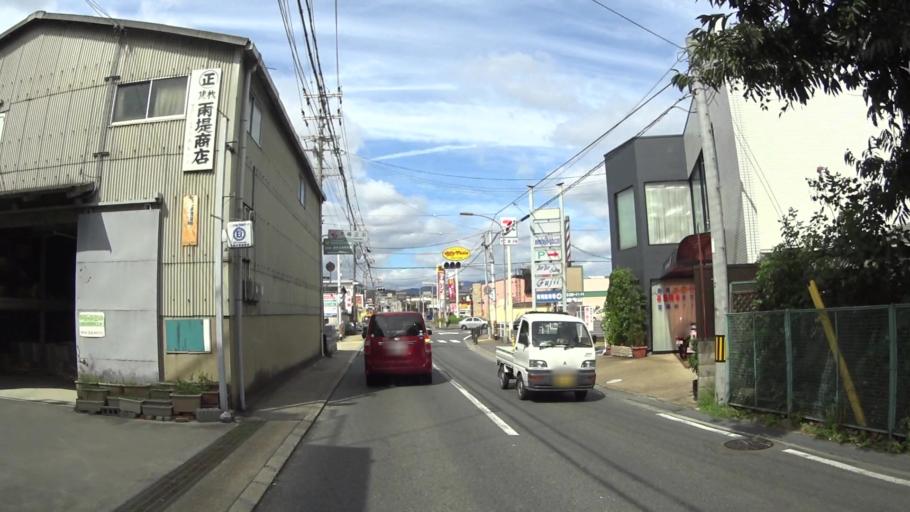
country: JP
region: Kyoto
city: Uji
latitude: 34.9283
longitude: 135.7997
